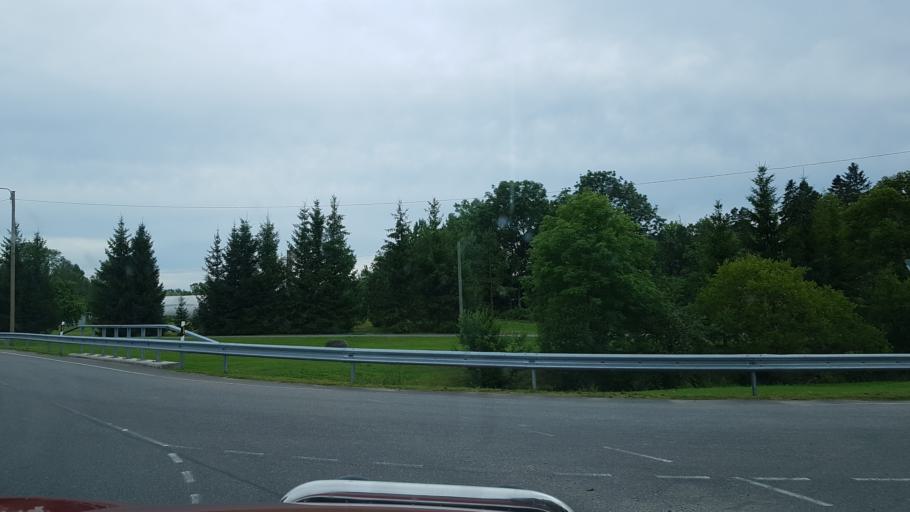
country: EE
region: Laeaene
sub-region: Lihula vald
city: Lihula
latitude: 58.8571
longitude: 23.7977
